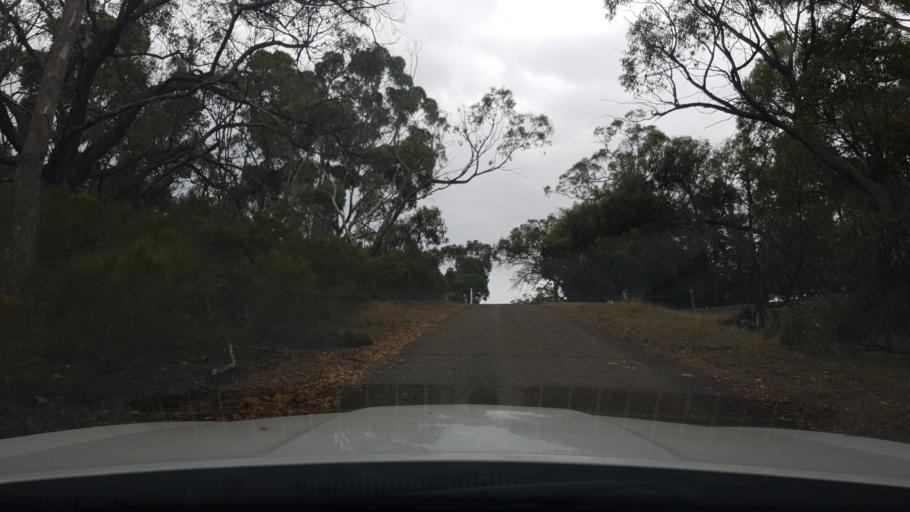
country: AU
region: Victoria
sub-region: Whittlesea
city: Whittlesea
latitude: -37.4895
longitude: 145.0521
